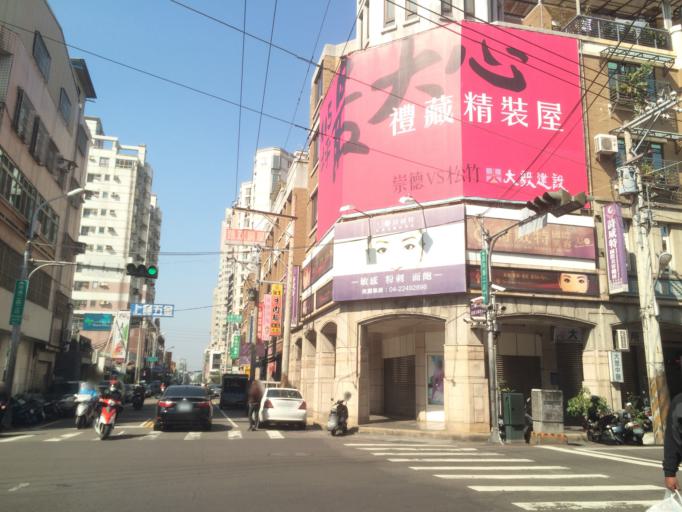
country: TW
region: Taiwan
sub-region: Taichung City
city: Taichung
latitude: 24.1768
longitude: 120.6907
